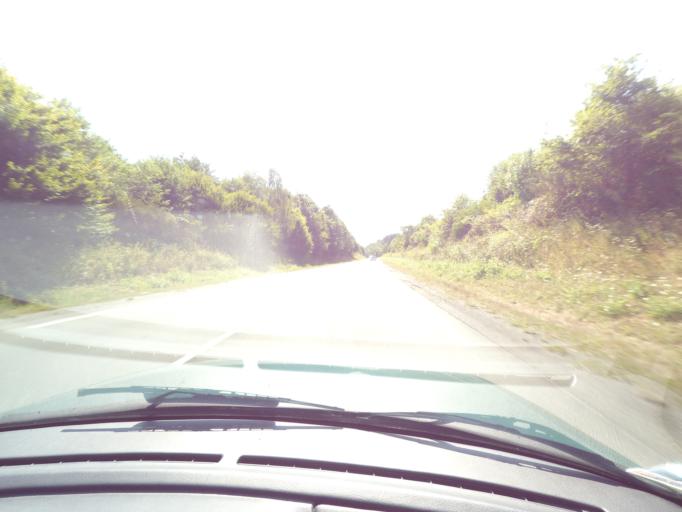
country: FR
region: Limousin
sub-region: Departement de la Haute-Vienne
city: Chaptelat
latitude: 45.8964
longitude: 1.2457
